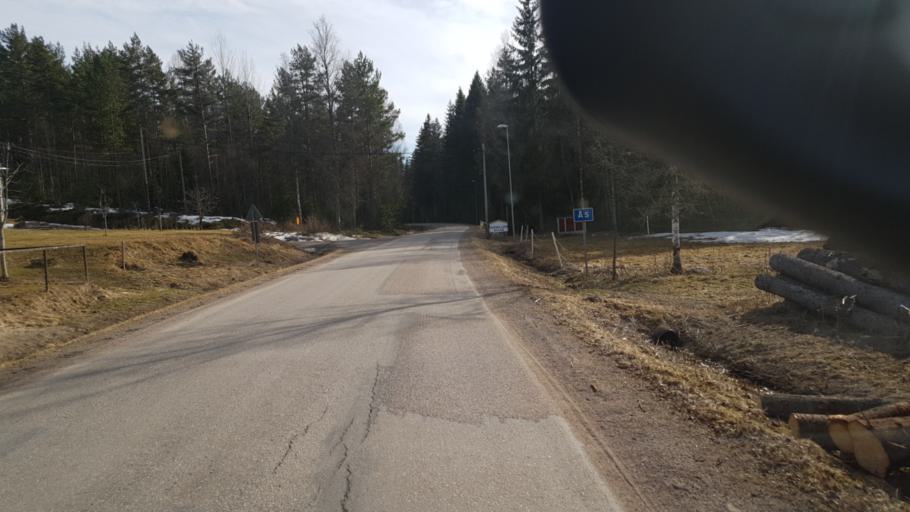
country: SE
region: Vaermland
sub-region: Eda Kommun
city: Charlottenberg
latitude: 59.8559
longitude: 12.3425
